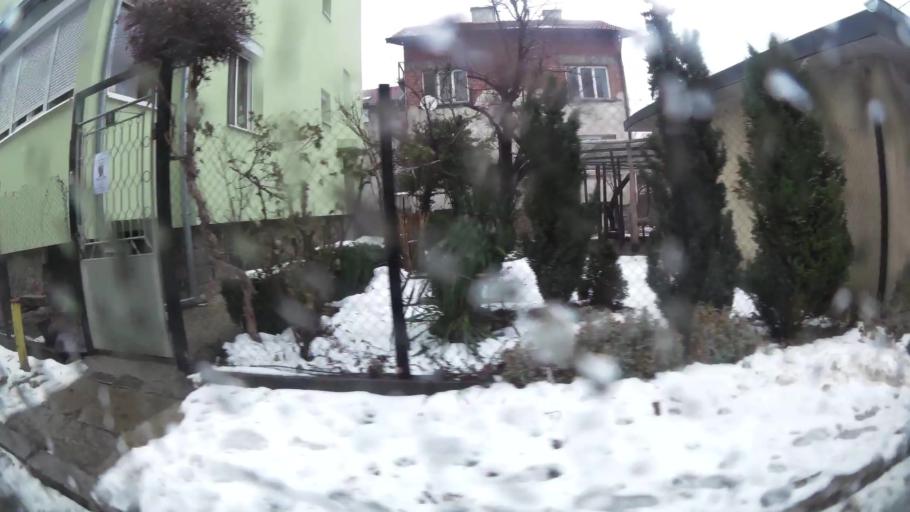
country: BG
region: Sofia-Capital
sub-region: Stolichna Obshtina
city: Sofia
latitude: 42.6807
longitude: 23.2654
